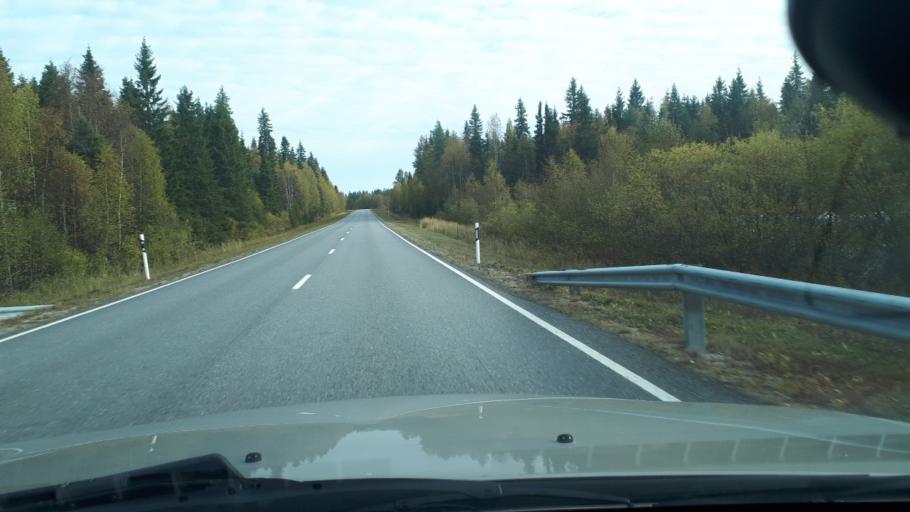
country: FI
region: Lapland
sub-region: Rovaniemi
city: Rovaniemi
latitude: 65.9564
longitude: 25.9347
